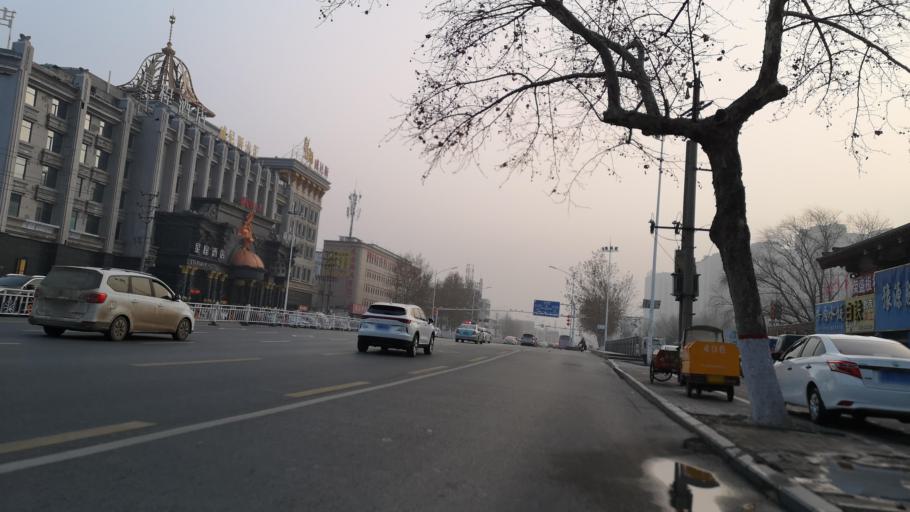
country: CN
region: Henan Sheng
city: Puyang
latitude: 35.7510
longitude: 115.0301
